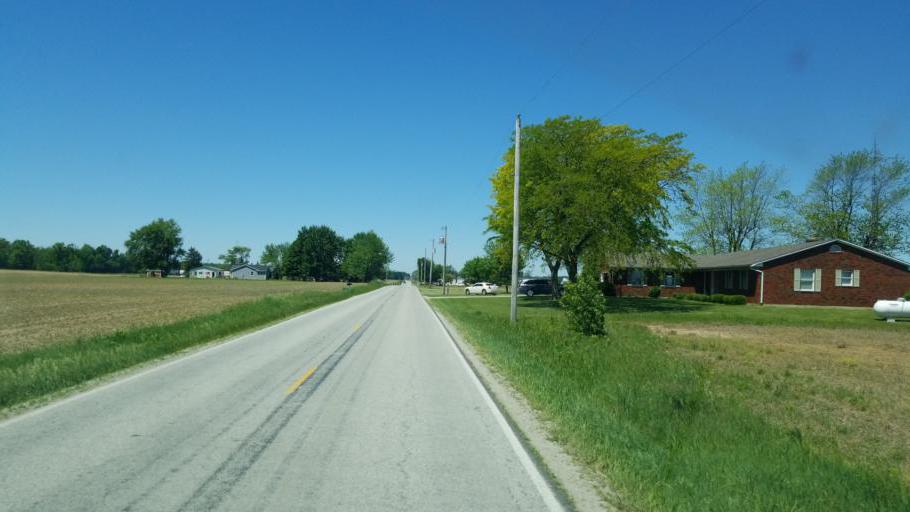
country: US
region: Ohio
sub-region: Shelby County
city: Fort Loramie
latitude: 40.3576
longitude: -84.3060
